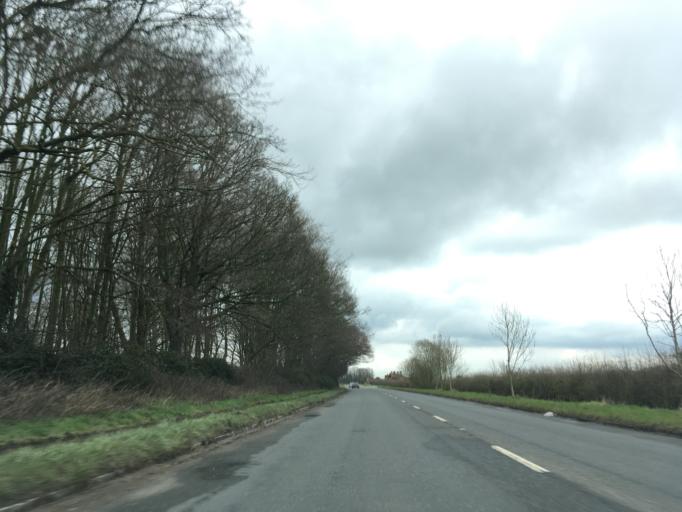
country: GB
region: England
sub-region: West Berkshire
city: Kintbury
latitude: 51.4136
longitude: -1.4285
